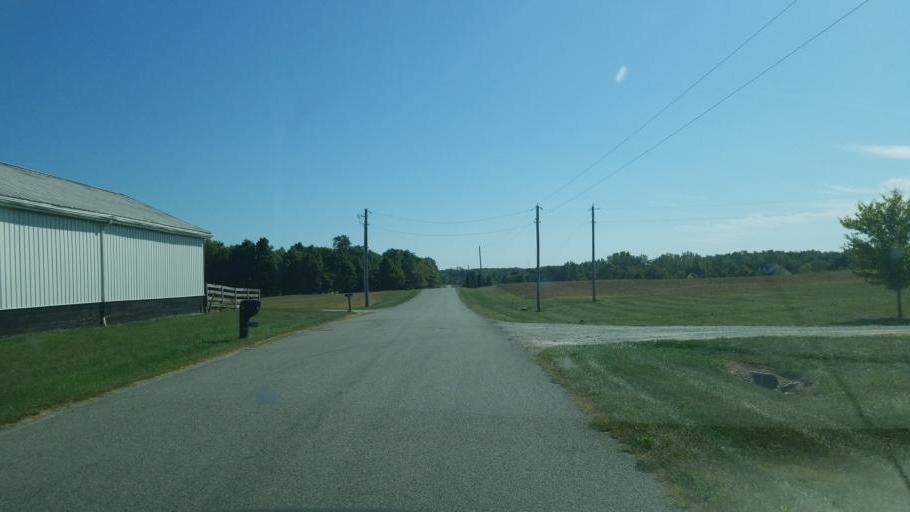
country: US
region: Ohio
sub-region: Champaign County
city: Mechanicsburg
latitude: 40.1269
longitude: -83.6002
